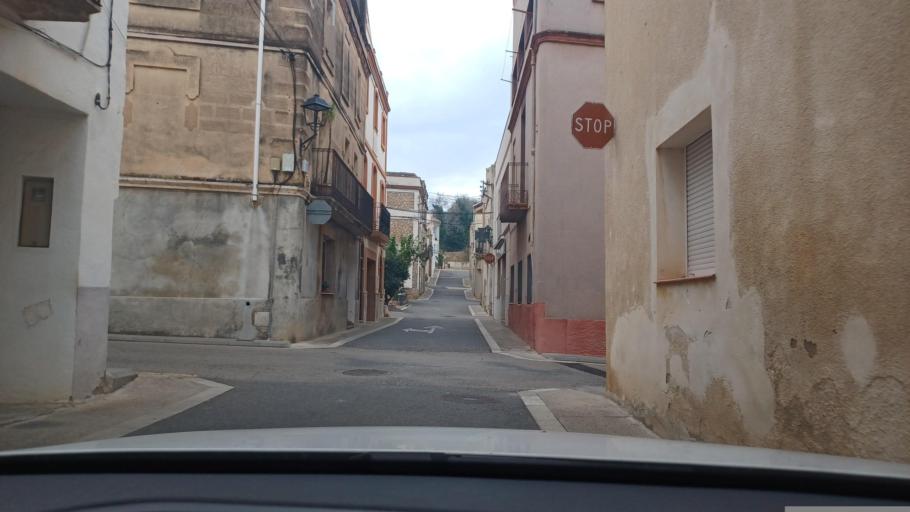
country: ES
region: Catalonia
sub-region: Provincia de Tarragona
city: Ulldecona
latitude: 40.6547
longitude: 0.4696
